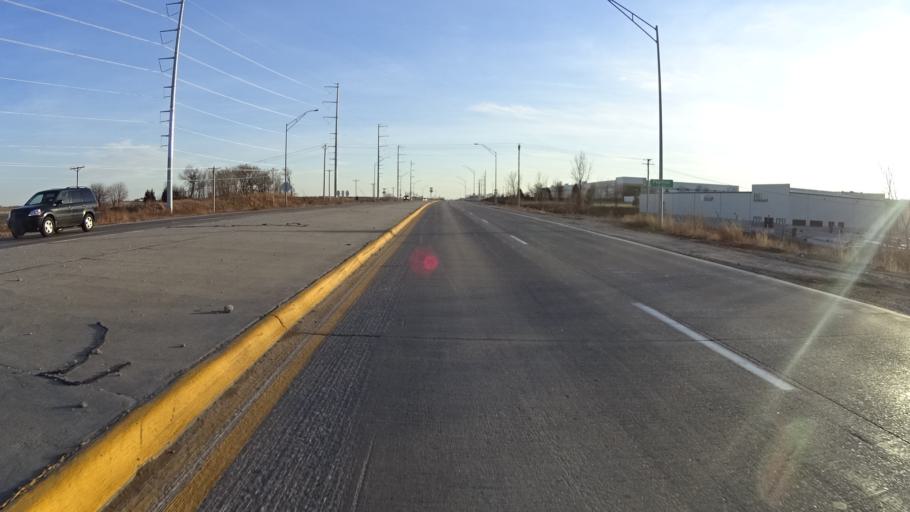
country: US
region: Nebraska
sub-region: Sarpy County
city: Chalco
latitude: 41.1463
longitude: -96.1391
